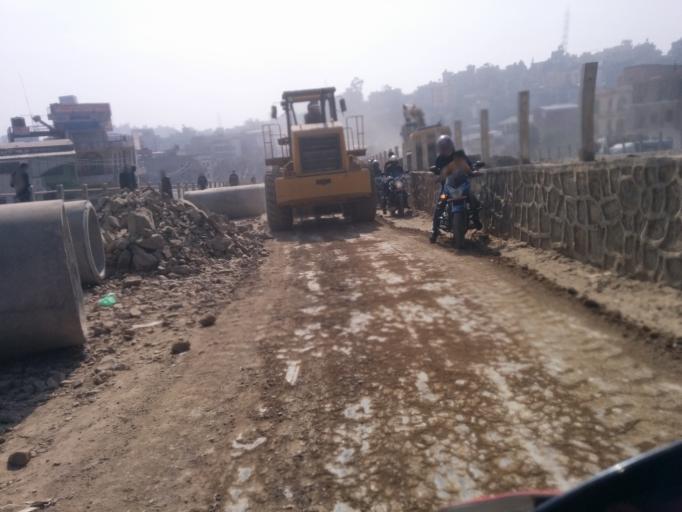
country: NP
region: Central Region
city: Kirtipur
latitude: 27.6915
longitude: 85.2827
